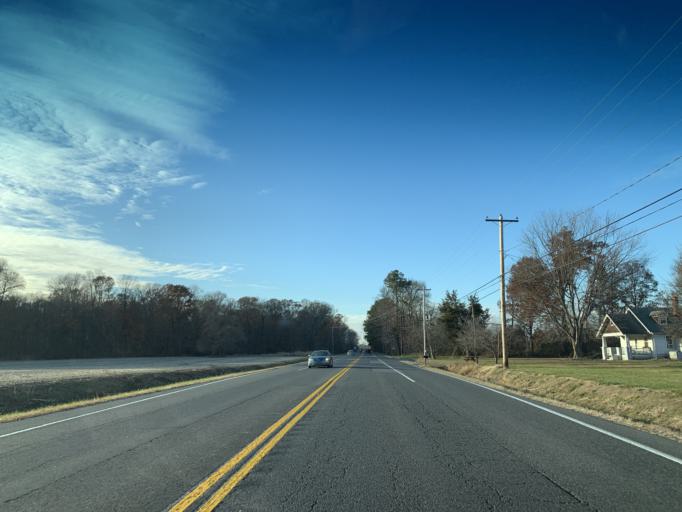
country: US
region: Maryland
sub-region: Queen Anne's County
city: Kingstown
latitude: 39.2003
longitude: -76.0431
